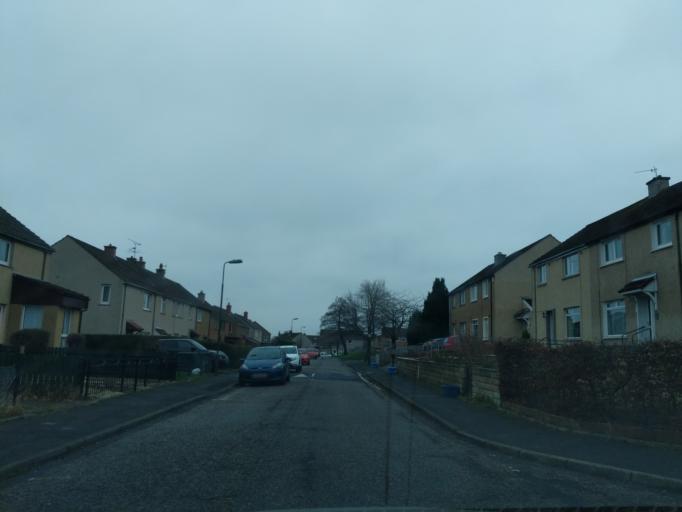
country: GB
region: Scotland
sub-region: Edinburgh
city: Currie
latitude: 55.8945
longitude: -3.3222
